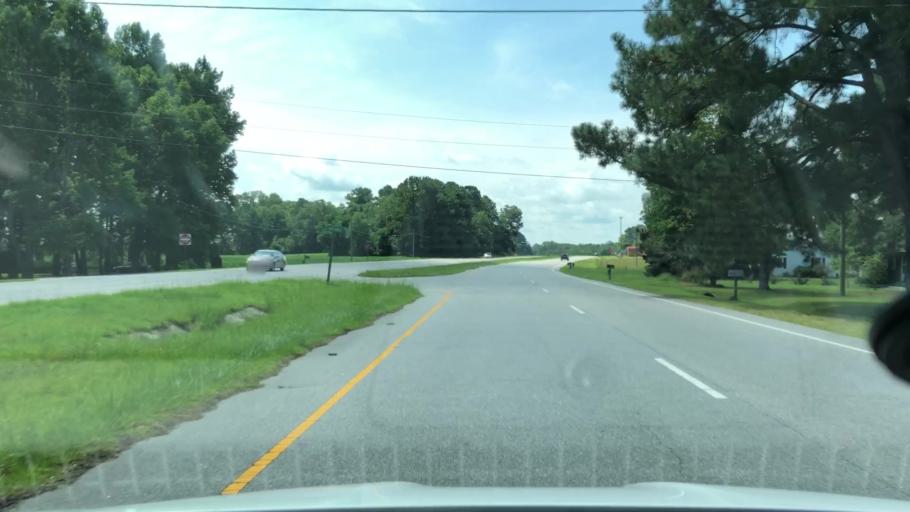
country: US
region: North Carolina
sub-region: Martin County
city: Williamston
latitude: 35.7990
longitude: -77.0597
